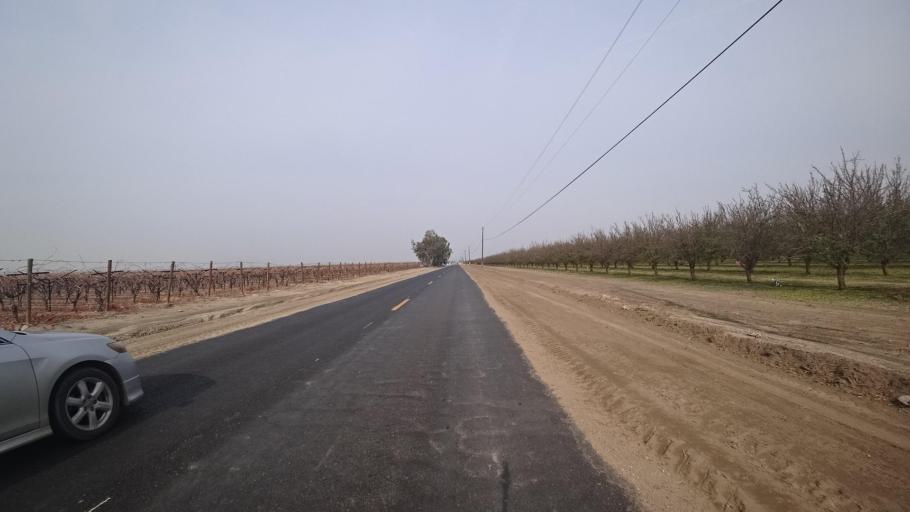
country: US
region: California
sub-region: Kern County
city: Arvin
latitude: 35.1408
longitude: -118.8507
